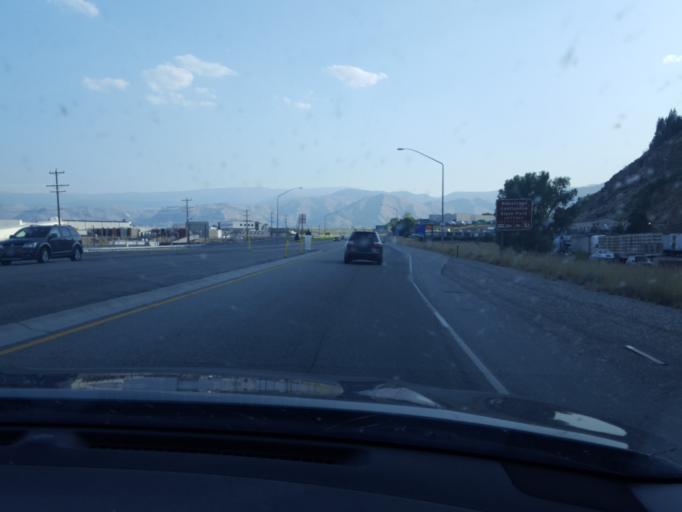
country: US
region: Washington
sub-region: Chelan County
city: Sunnyslope
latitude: 47.4803
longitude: -120.3213
